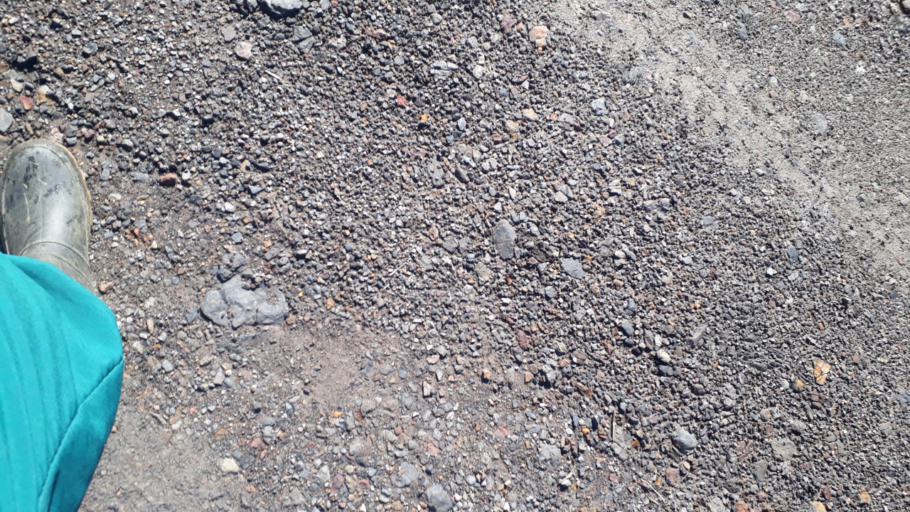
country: CO
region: Casanare
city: Nunchia
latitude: 5.6631
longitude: -72.4227
